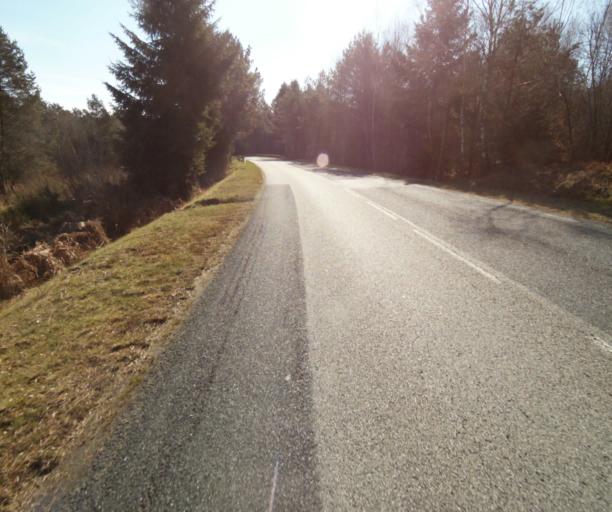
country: FR
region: Limousin
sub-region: Departement de la Correze
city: Correze
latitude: 45.2809
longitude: 1.9259
